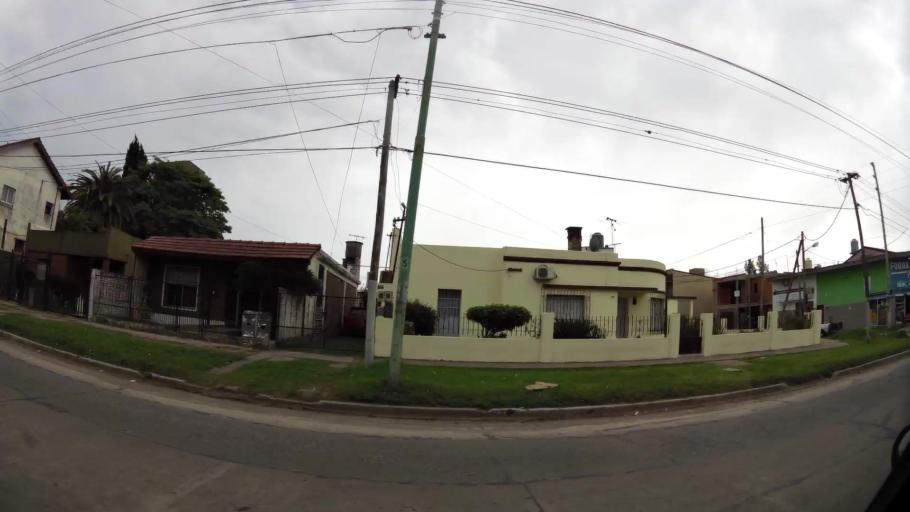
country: AR
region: Buenos Aires
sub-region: Partido de Quilmes
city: Quilmes
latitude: -34.7917
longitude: -58.2482
